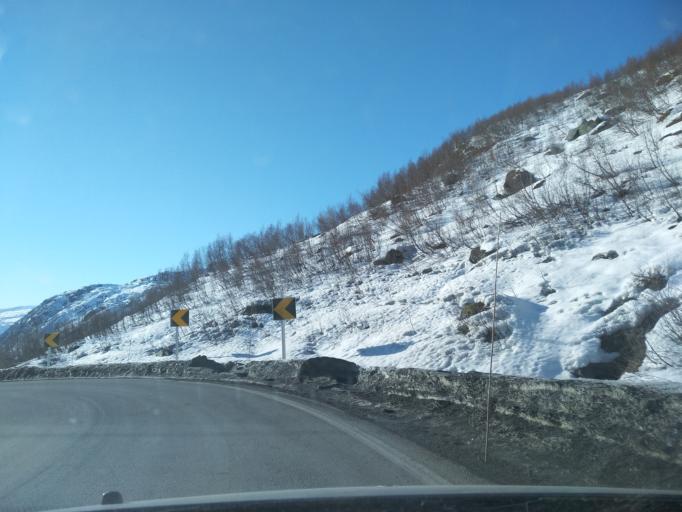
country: NO
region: Hordaland
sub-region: Odda
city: Odda
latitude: 59.8572
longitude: 6.8846
